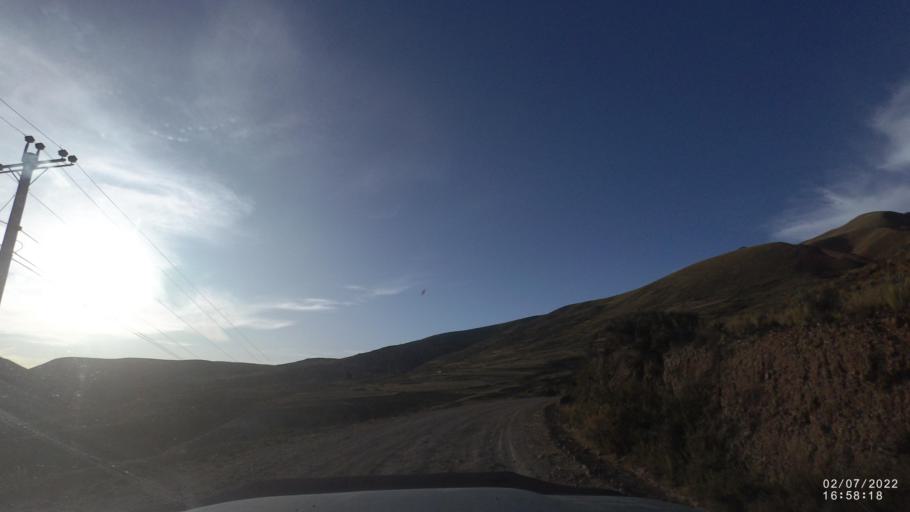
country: BO
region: Cochabamba
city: Irpa Irpa
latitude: -17.9471
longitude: -66.5480
